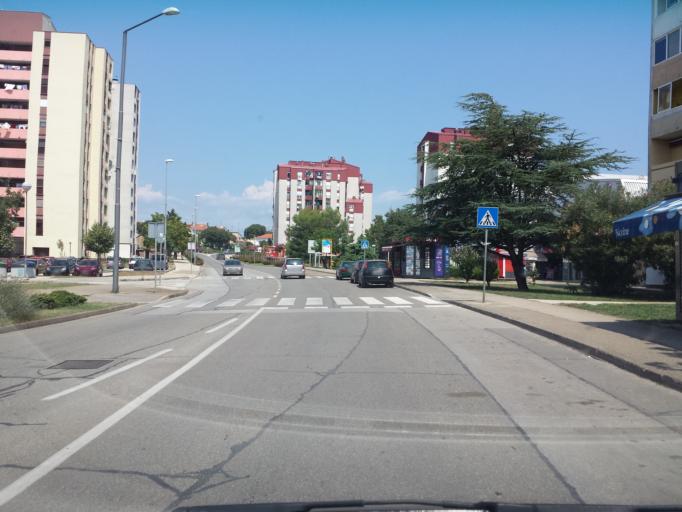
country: HR
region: Istarska
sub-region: Grad Pula
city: Pula
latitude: 44.8766
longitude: 13.8602
